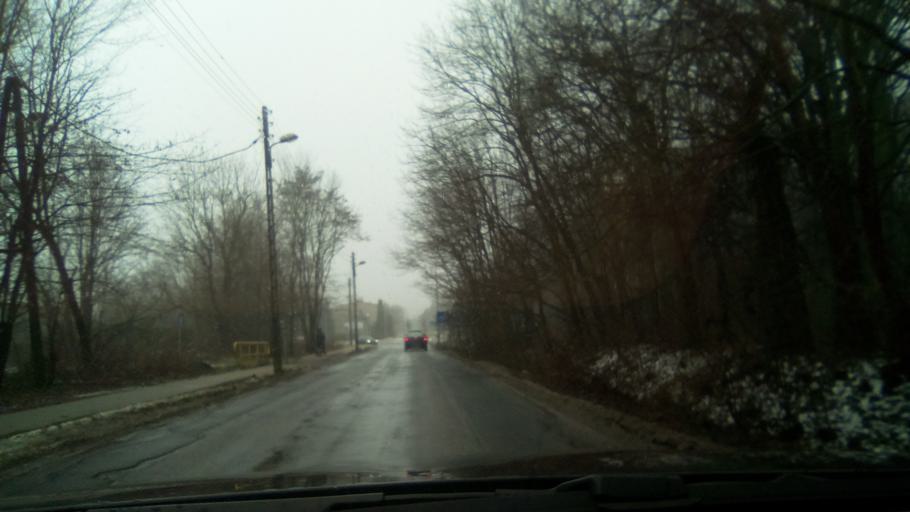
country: PL
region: Greater Poland Voivodeship
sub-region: Powiat poznanski
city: Swarzedz
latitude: 52.3923
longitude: 17.0141
